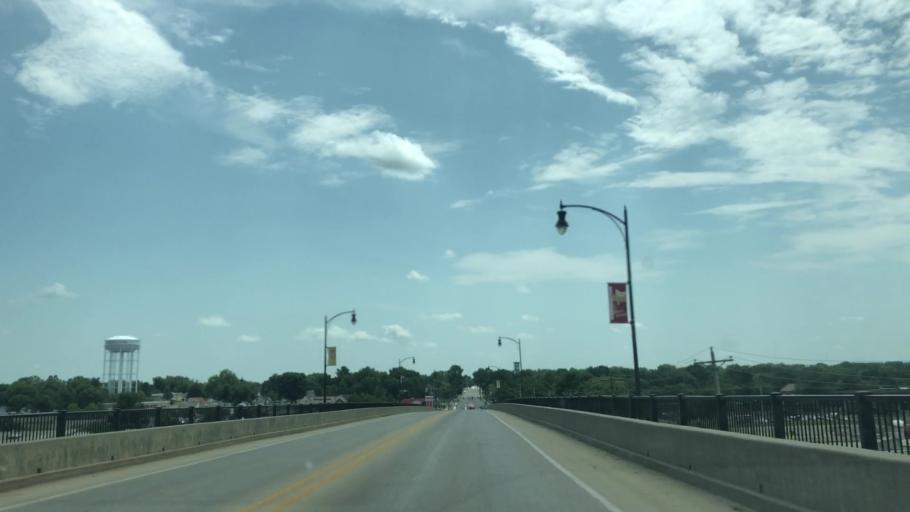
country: US
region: Iowa
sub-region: Marshall County
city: Marshalltown
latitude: 42.0427
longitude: -92.9129
